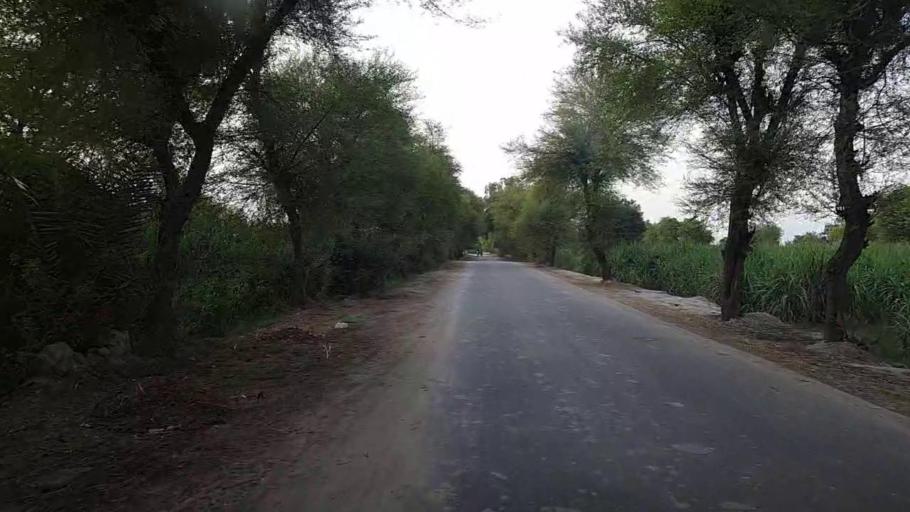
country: PK
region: Sindh
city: Ubauro
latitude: 28.2879
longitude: 69.8001
